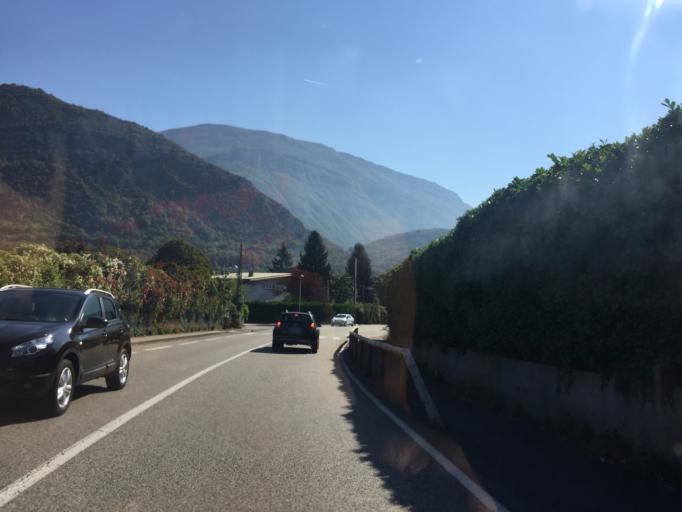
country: FR
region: Rhone-Alpes
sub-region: Departement de la Savoie
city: Challes-les-Eaux
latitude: 45.5440
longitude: 5.9831
